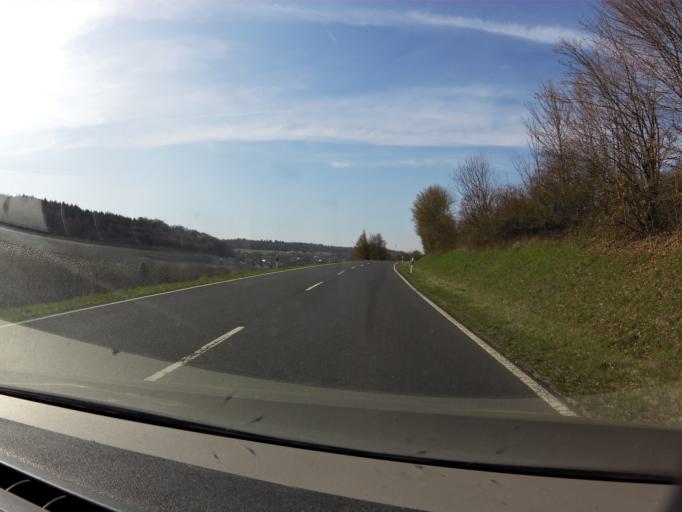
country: DE
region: Baden-Wuerttemberg
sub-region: Regierungsbezirk Stuttgart
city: Creglingen
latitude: 49.4658
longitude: 10.0463
